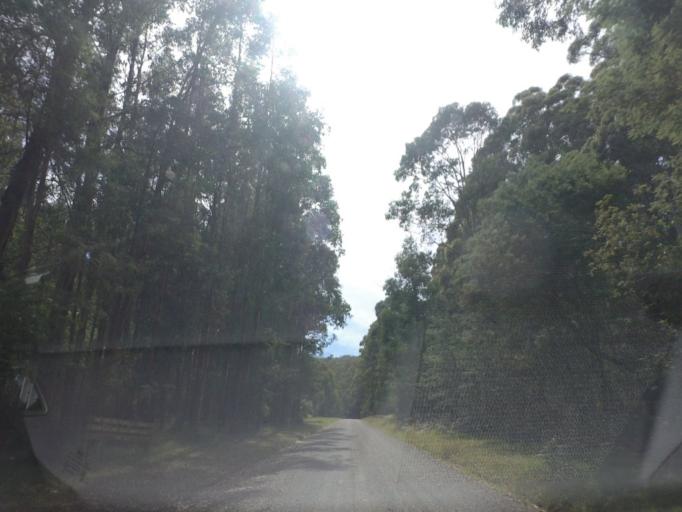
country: AU
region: Victoria
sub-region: Yarra Ranges
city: Healesville
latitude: -37.5560
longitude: 145.5089
